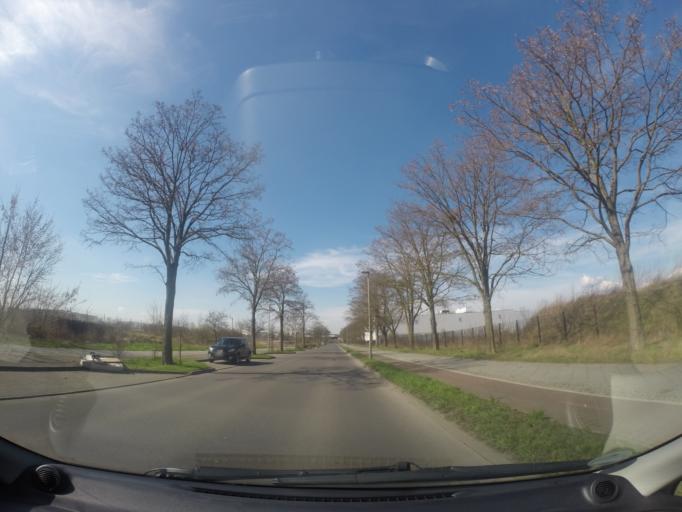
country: DE
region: Berlin
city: Falkenberg
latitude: 52.5639
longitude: 13.5442
